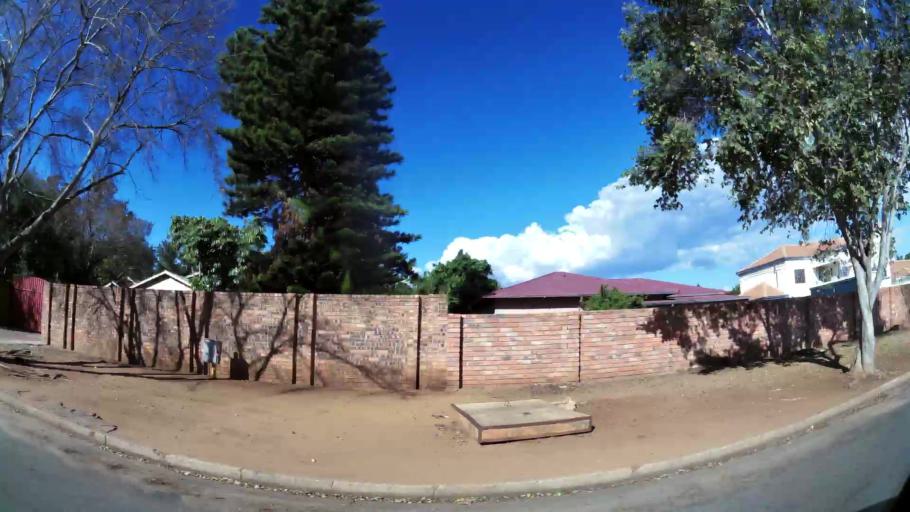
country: ZA
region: Limpopo
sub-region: Waterberg District Municipality
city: Mokopane
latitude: -24.1791
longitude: 29.0012
